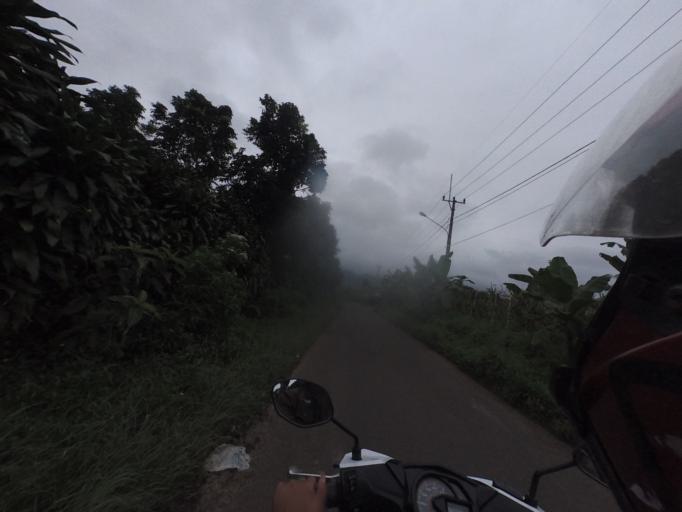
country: ID
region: West Java
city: Bogor
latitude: -6.6519
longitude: 106.7278
